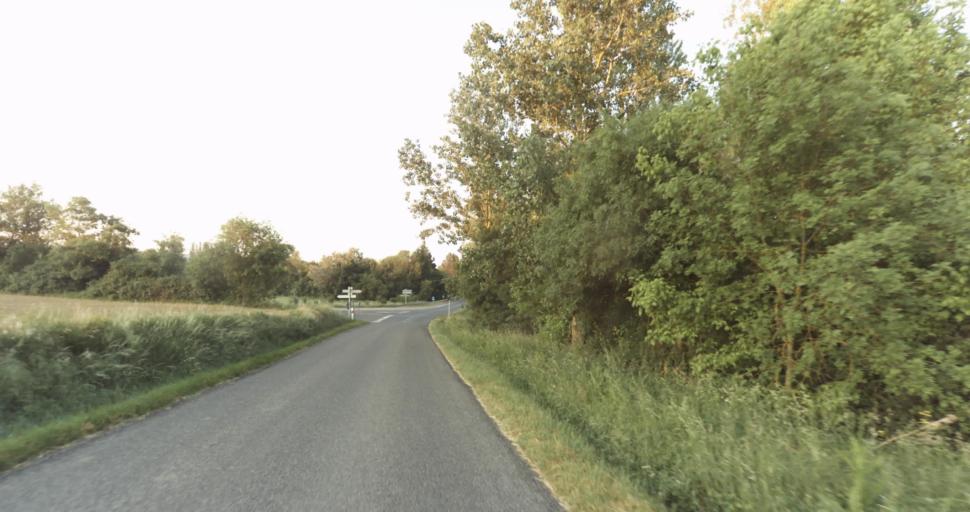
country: FR
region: Midi-Pyrenees
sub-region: Departement du Gers
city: Pujaudran
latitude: 43.6415
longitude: 1.1081
